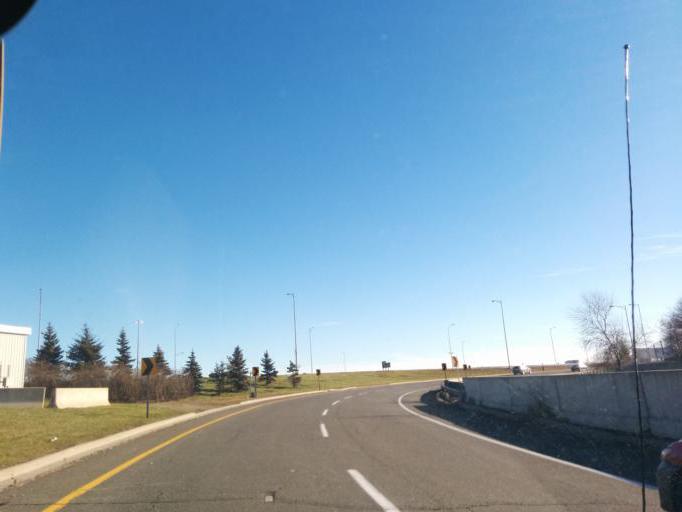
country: CA
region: Ontario
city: Etobicoke
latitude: 43.6959
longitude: -79.6082
